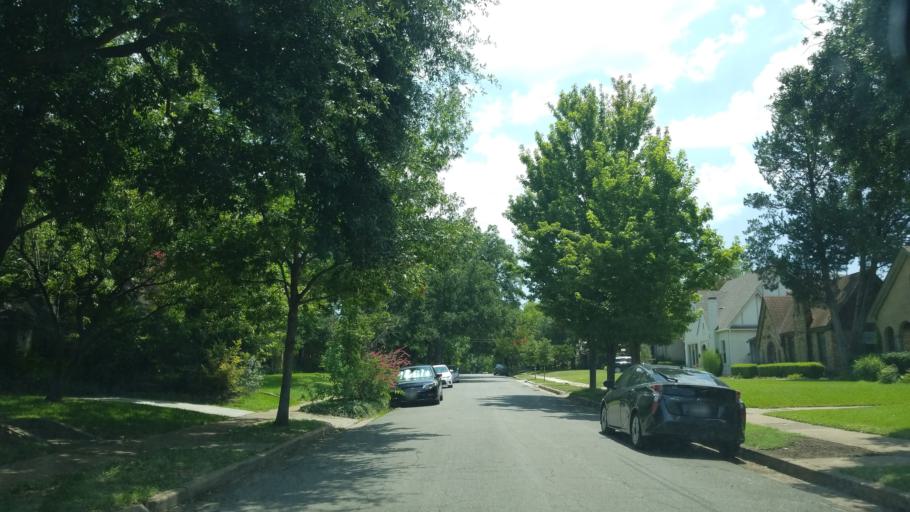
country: US
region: Texas
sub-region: Dallas County
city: Highland Park
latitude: 32.8255
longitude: -96.7786
